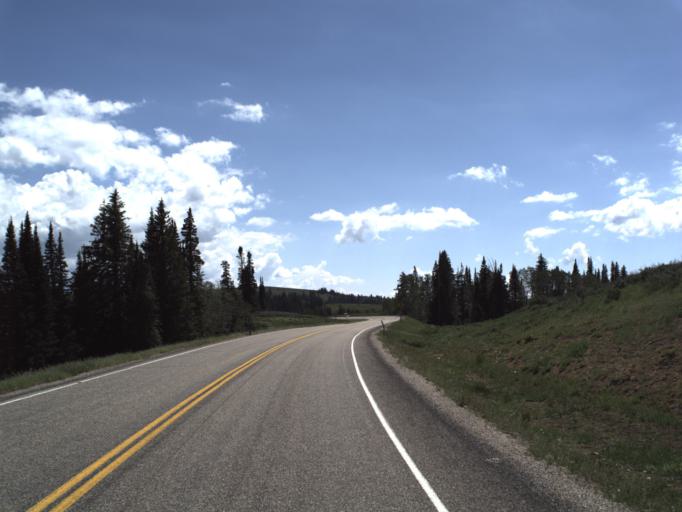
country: US
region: Utah
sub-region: Weber County
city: Wolf Creek
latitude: 41.4479
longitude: -111.5034
